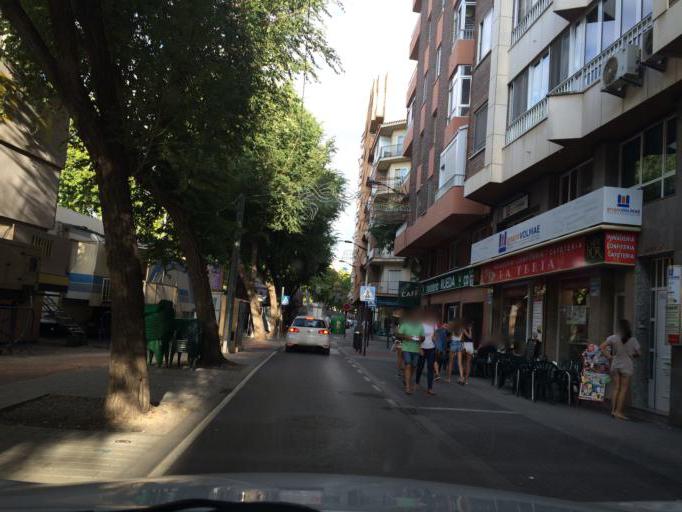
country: ES
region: Castille-La Mancha
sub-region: Provincia de Albacete
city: Albacete
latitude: 38.9963
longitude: -1.8652
